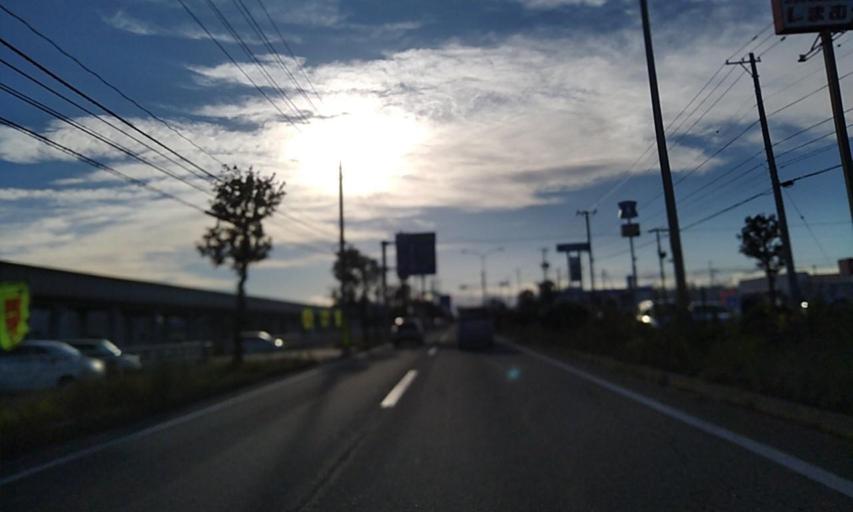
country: JP
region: Hokkaido
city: Obihiro
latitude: 42.9293
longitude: 143.1680
